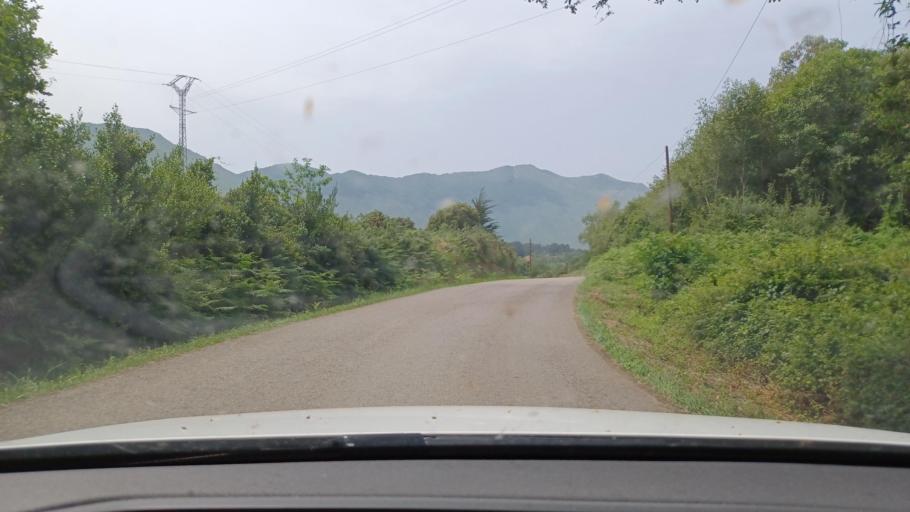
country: ES
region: Asturias
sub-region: Province of Asturias
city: Ribadesella
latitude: 43.4475
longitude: -4.9789
